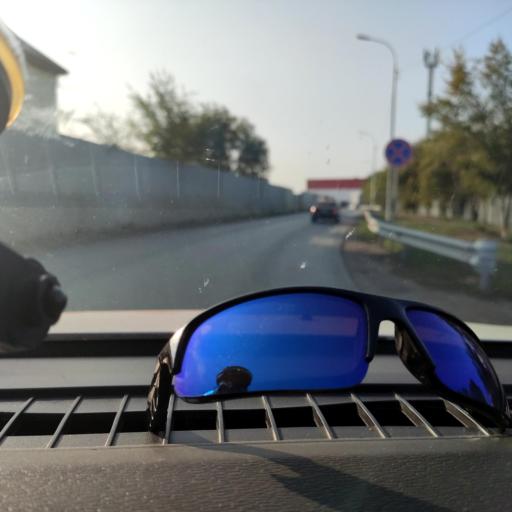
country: RU
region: Samara
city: Samara
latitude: 53.0970
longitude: 50.1382
